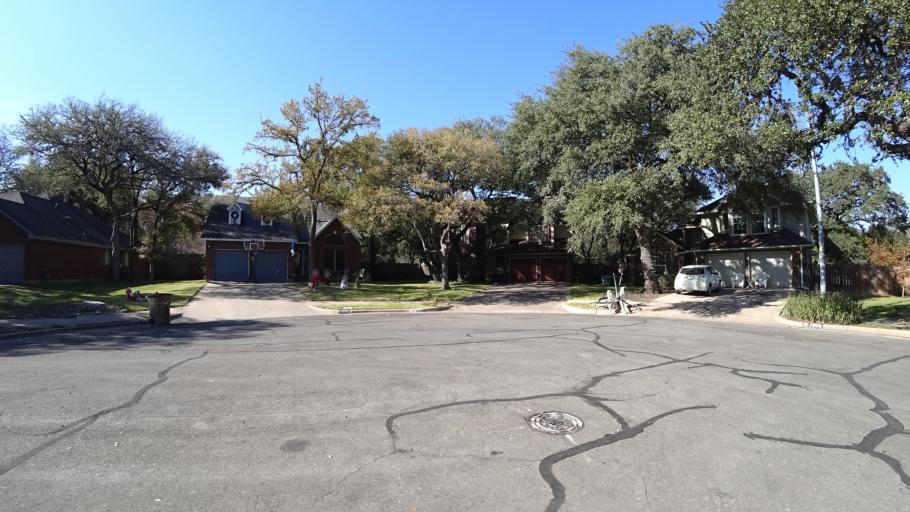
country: US
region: Texas
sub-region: Travis County
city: Barton Creek
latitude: 30.2253
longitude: -97.8624
